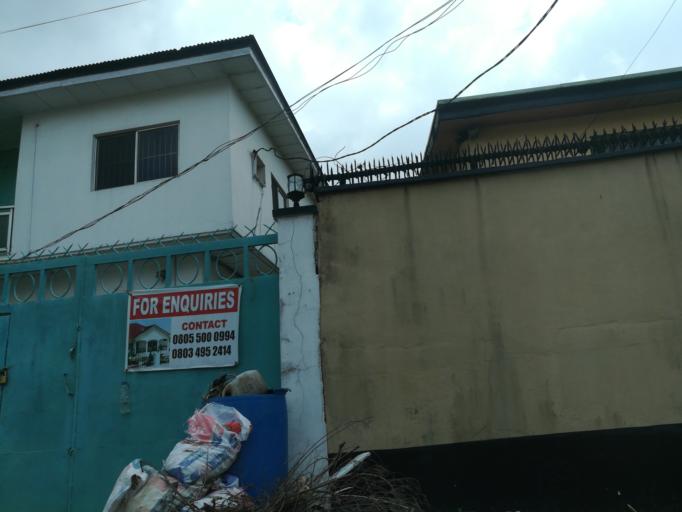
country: NG
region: Lagos
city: Oshodi
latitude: 6.5440
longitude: 3.3316
